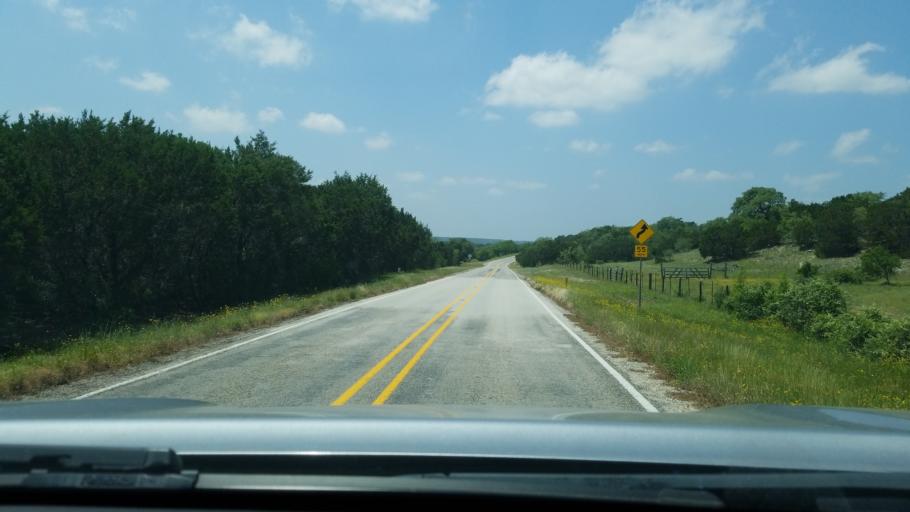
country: US
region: Texas
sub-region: Hays County
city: Woodcreek
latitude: 30.0928
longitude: -98.2314
